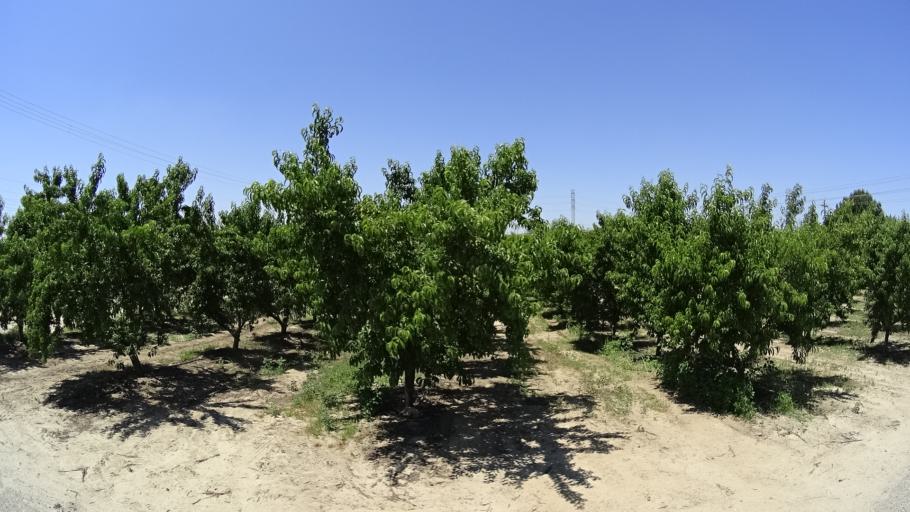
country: US
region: California
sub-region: Fresno County
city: Kingsburg
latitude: 36.4886
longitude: -119.5910
